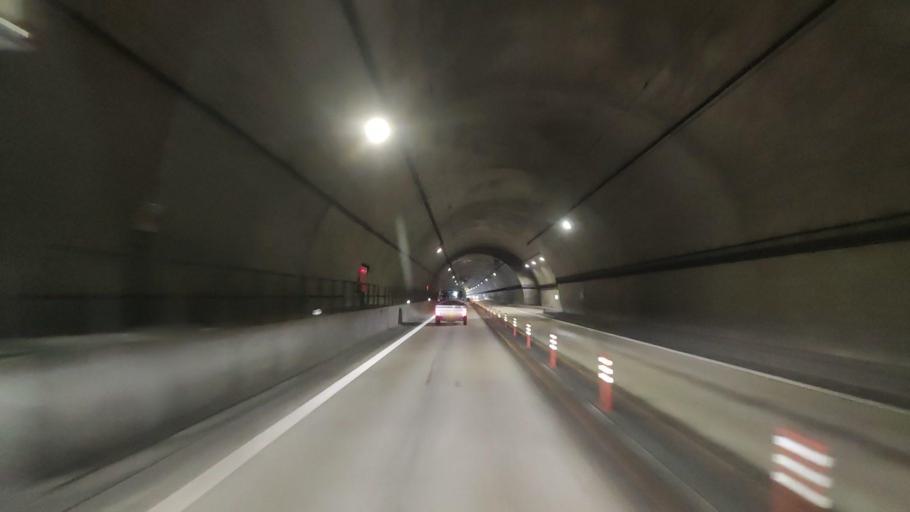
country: JP
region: Wakayama
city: Tanabe
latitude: 33.6282
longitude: 135.4156
